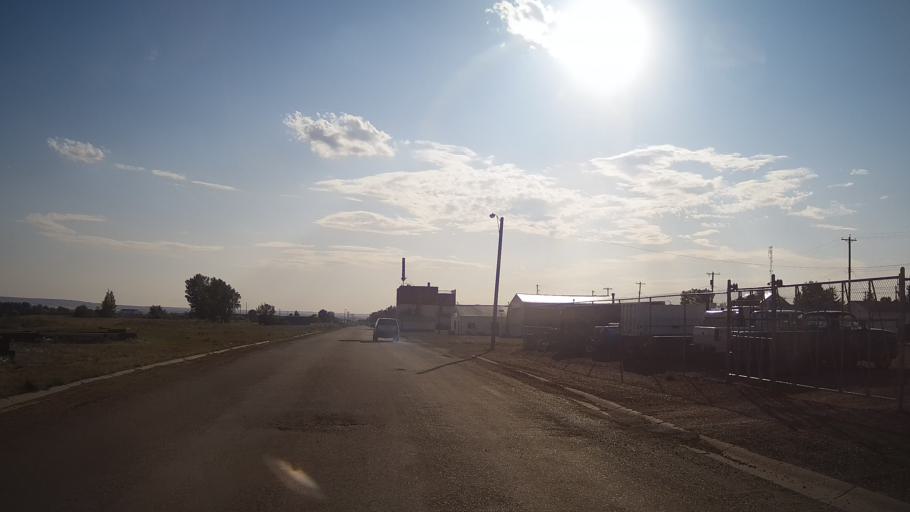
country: CA
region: Alberta
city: Hanna
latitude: 51.6424
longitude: -111.9213
